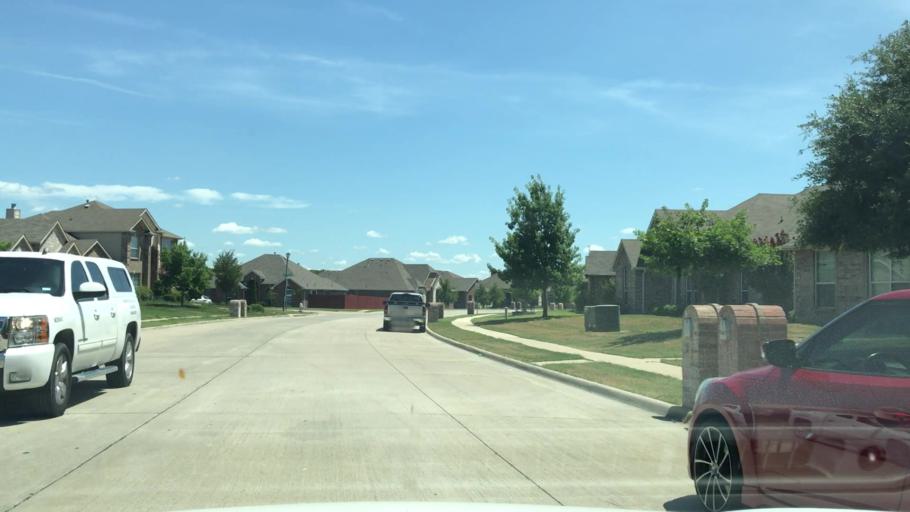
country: US
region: Texas
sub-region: Rockwall County
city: Rockwall
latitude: 32.8931
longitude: -96.4563
